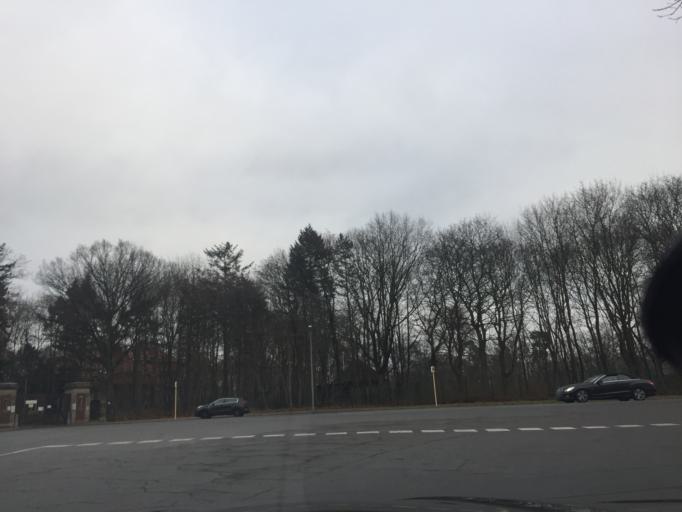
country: DE
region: Berlin
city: Haselhorst
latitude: 52.5112
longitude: 13.2307
